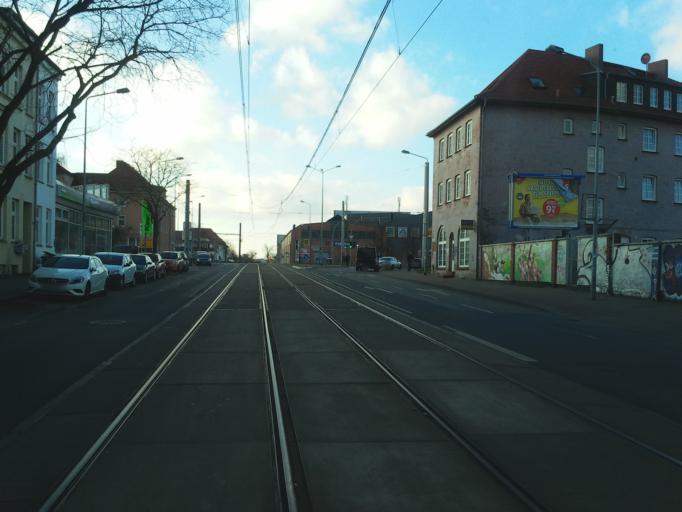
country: DE
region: Mecklenburg-Vorpommern
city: Rostock
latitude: 54.0924
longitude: 12.1108
